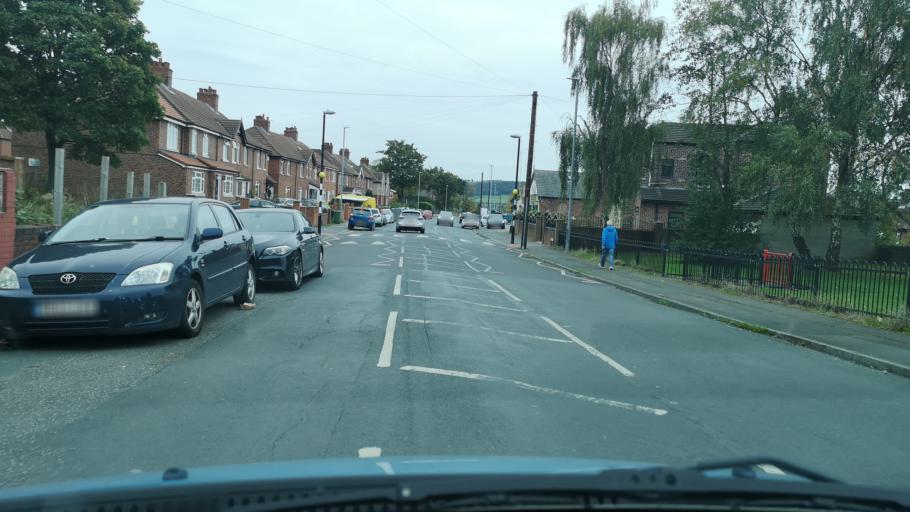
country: GB
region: England
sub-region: Kirklees
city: Batley
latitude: 53.6887
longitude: -1.6563
